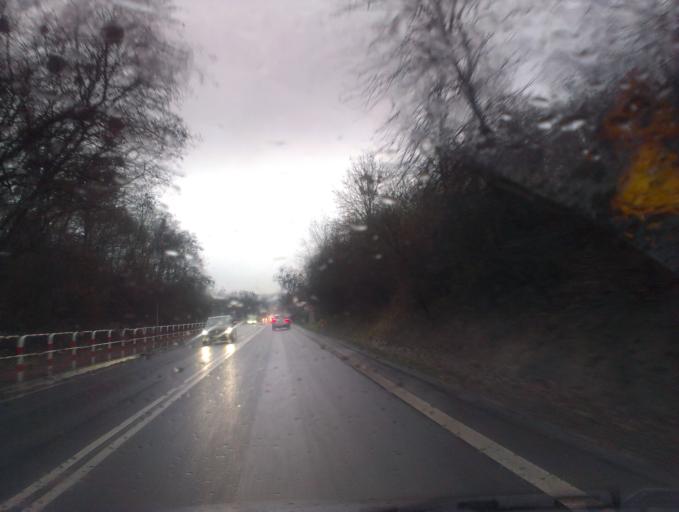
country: PL
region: Greater Poland Voivodeship
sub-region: Powiat obornicki
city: Oborniki
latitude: 52.6317
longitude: 16.8098
